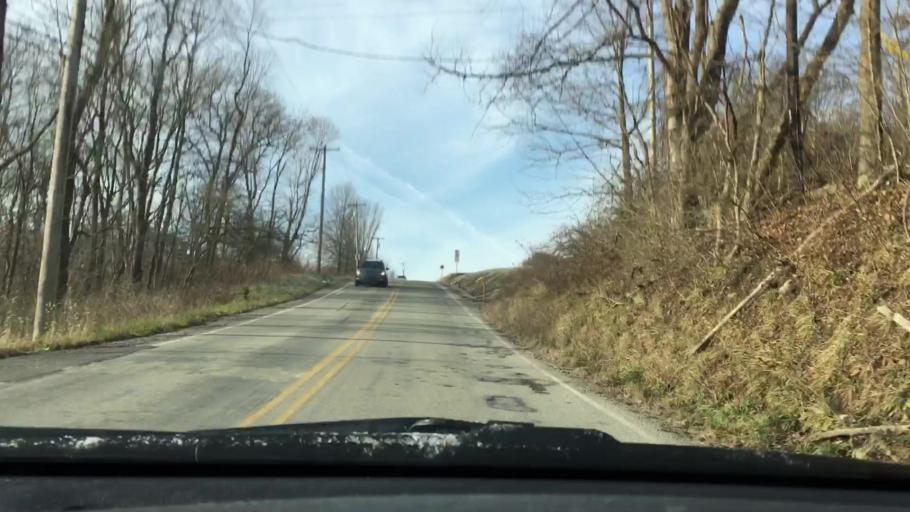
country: US
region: Pennsylvania
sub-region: Westmoreland County
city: Collinsburg
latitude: 40.2602
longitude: -79.7282
